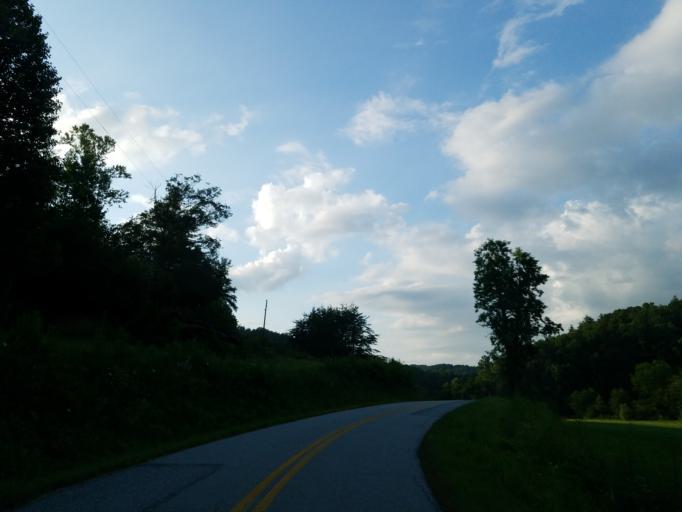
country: US
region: Georgia
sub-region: Lumpkin County
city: Dahlonega
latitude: 34.6966
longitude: -84.0794
